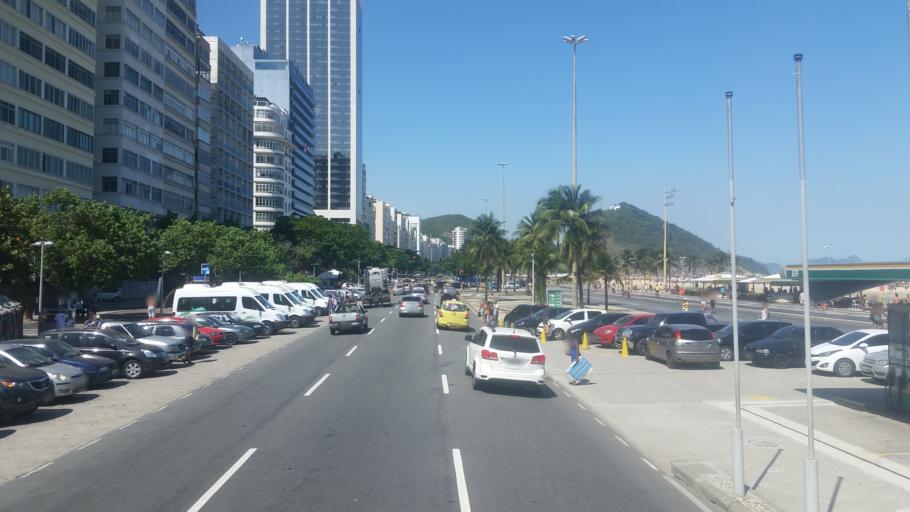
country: BR
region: Rio de Janeiro
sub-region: Rio De Janeiro
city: Rio de Janeiro
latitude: -22.9660
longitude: -43.1756
